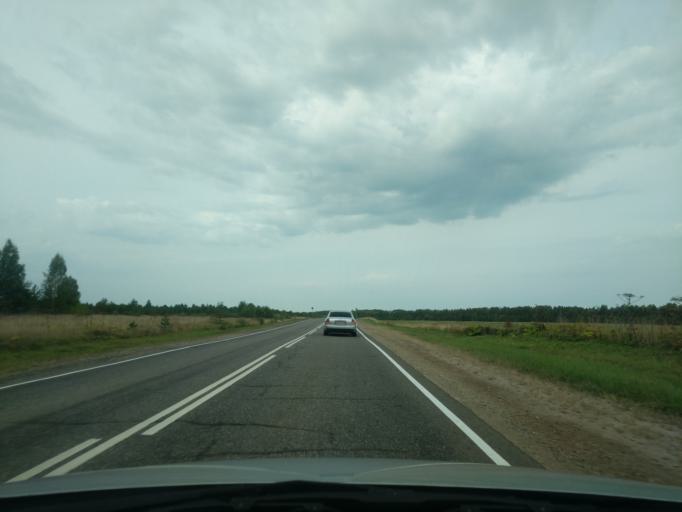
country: RU
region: Kirov
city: Mirnyy
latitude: 58.2733
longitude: 47.7716
